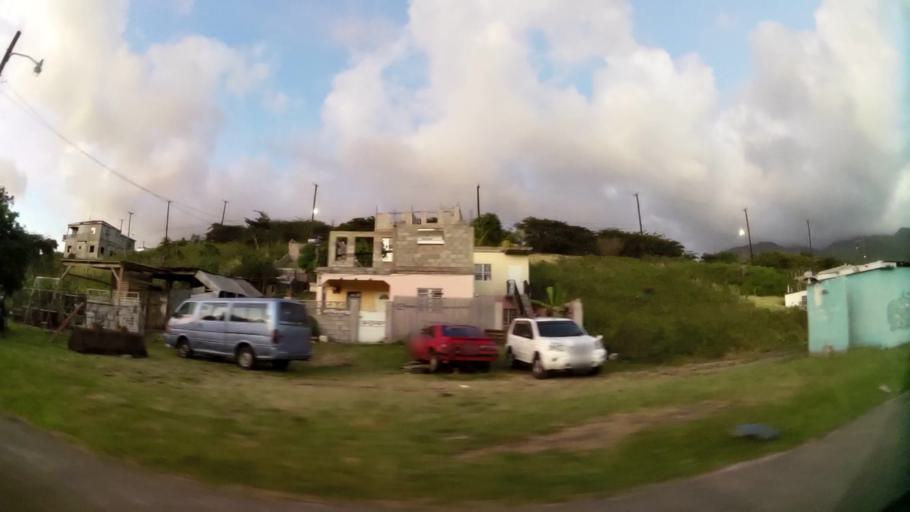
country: KN
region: Saint Thomas Middle Island
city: Middle Island
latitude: 17.3253
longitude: -62.8104
